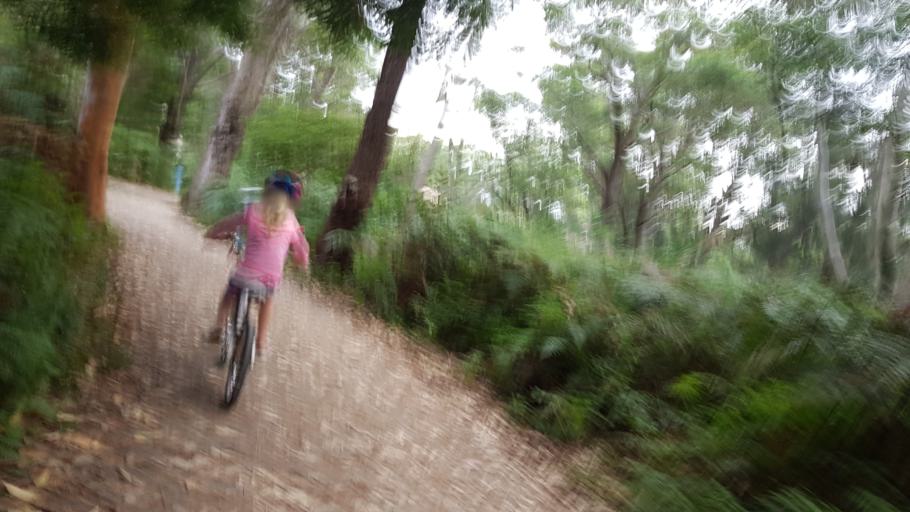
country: AU
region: New South Wales
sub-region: Warringah
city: Narrabeen
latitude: -33.7213
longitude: 151.2777
